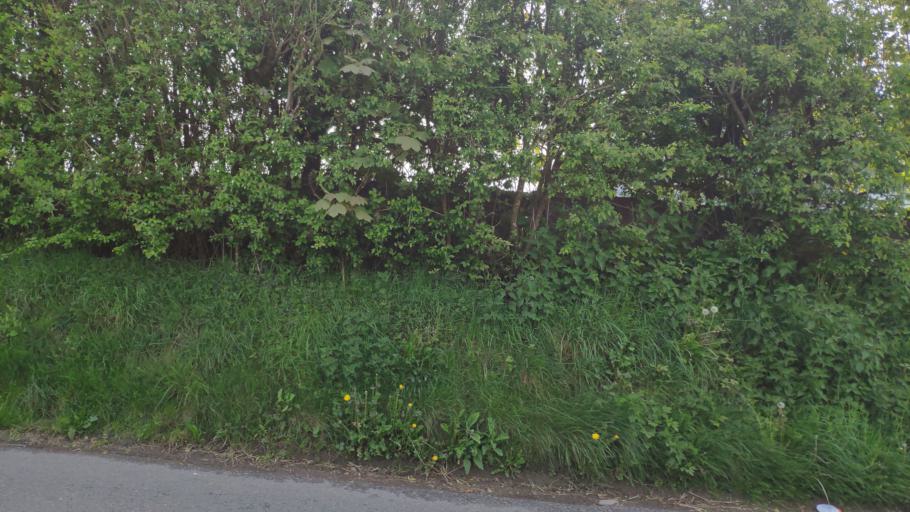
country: IE
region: Munster
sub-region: County Cork
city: Blarney
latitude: 51.9838
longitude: -8.5131
